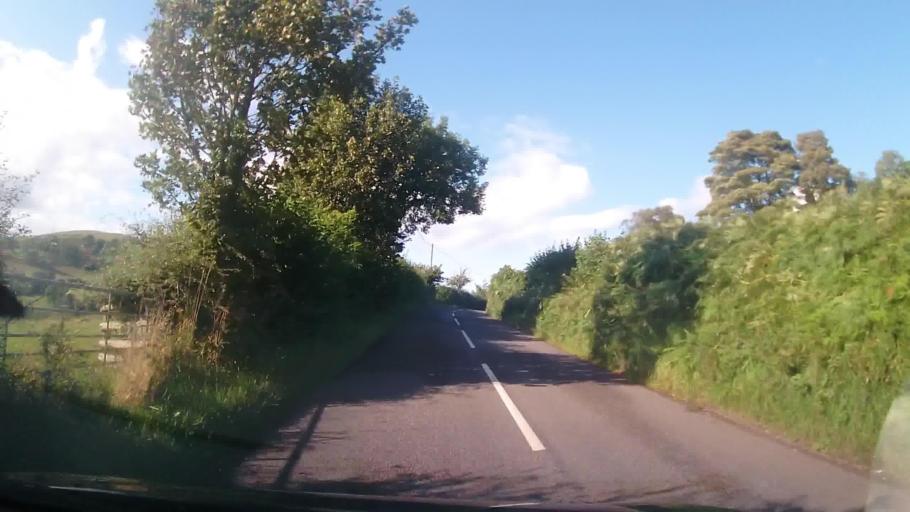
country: GB
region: England
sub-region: Shropshire
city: Norbury
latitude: 52.5691
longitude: -2.8926
